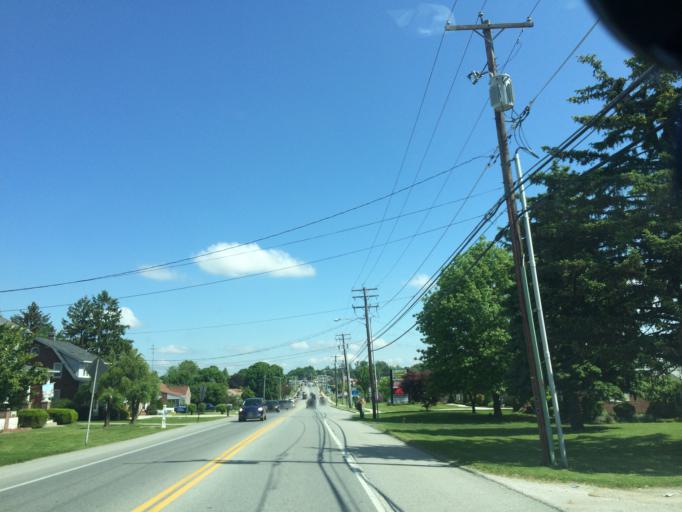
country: US
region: Pennsylvania
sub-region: York County
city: Parkville
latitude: 39.7686
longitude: -76.9607
